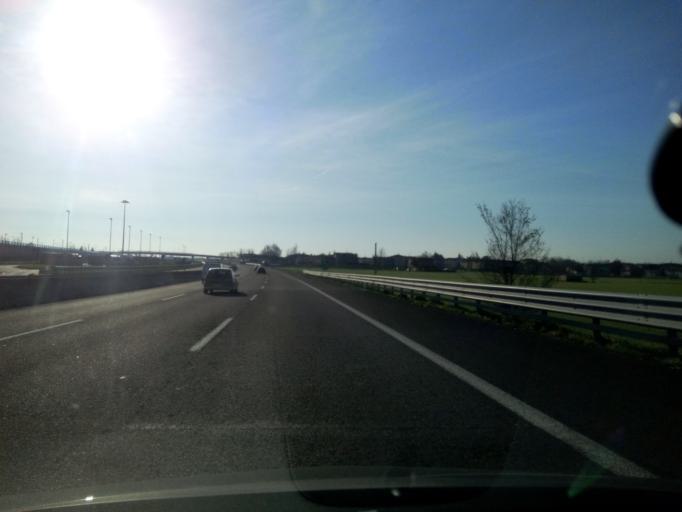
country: IT
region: Emilia-Romagna
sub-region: Provincia di Reggio Emilia
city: Roncocesi
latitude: 44.7434
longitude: 10.5714
